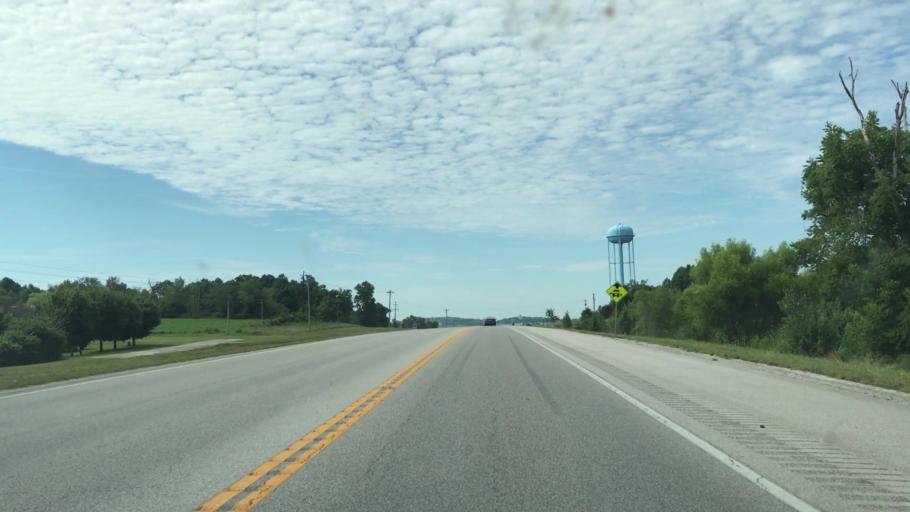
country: US
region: Kentucky
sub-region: Edmonson County
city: Brownsville
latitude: 37.1052
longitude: -86.2295
